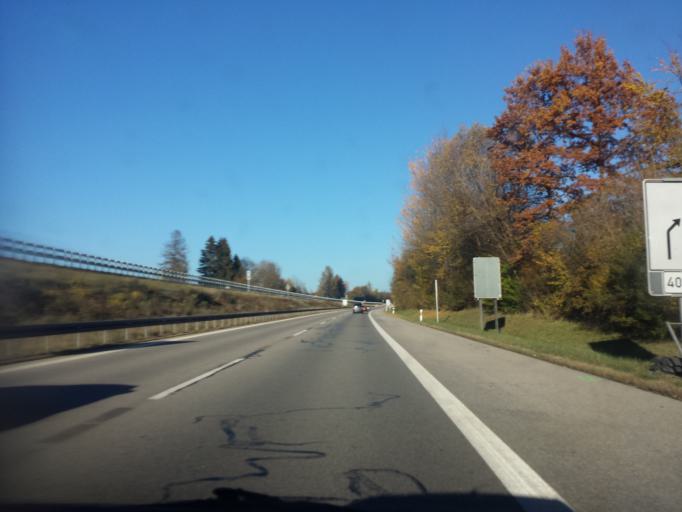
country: DE
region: Bavaria
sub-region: Upper Bavaria
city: Ohlstadt
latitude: 47.6527
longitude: 11.2301
